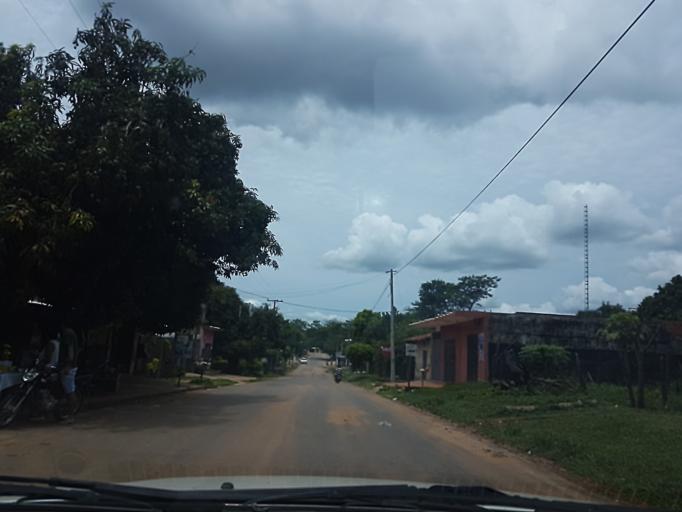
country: PY
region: Central
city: Colonia Mariano Roque Alonso
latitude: -25.1869
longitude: -57.5284
